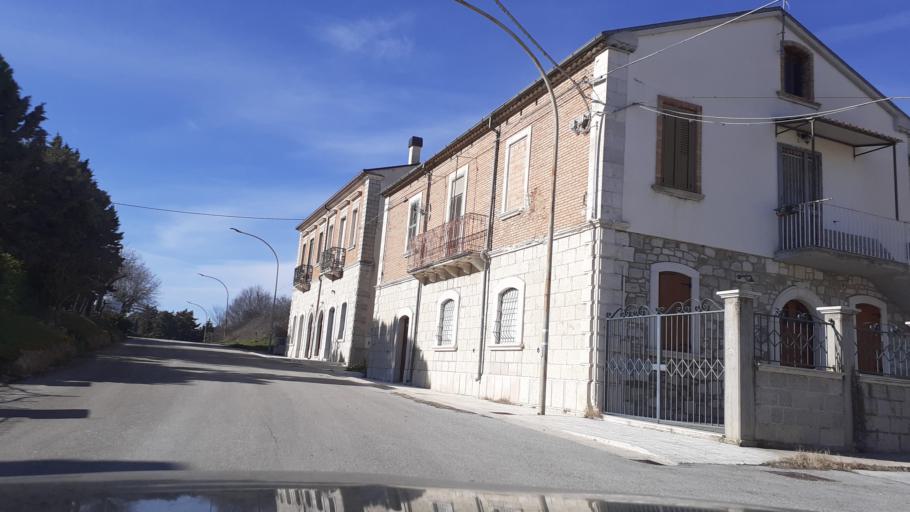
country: IT
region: Molise
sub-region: Provincia di Campobasso
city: Pietracupa
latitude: 41.6827
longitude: 14.5168
